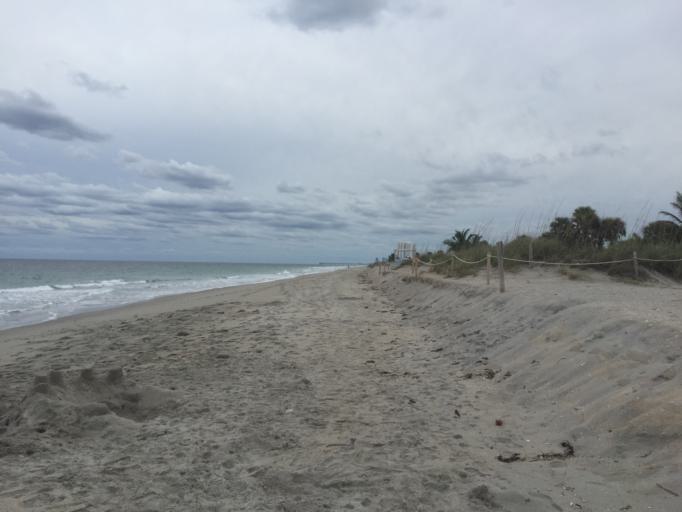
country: US
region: Florida
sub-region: Broward County
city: Dania Beach
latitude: 26.0817
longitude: -80.1096
